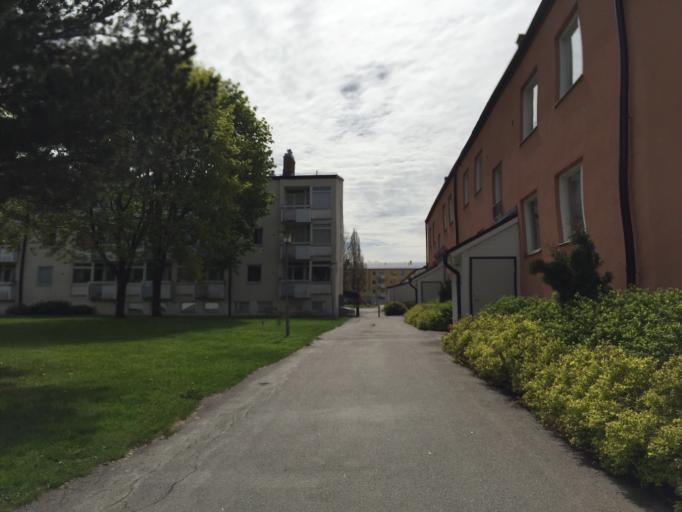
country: SE
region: Dalarna
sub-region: Ludvika Kommun
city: Ludvika
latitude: 60.1332
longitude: 15.1811
